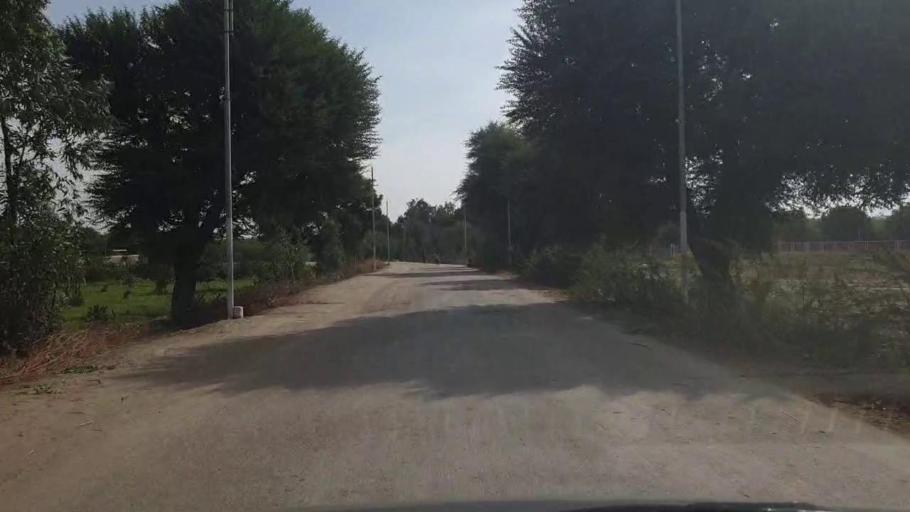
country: PK
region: Sindh
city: Umarkot
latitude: 25.2858
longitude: 69.7136
